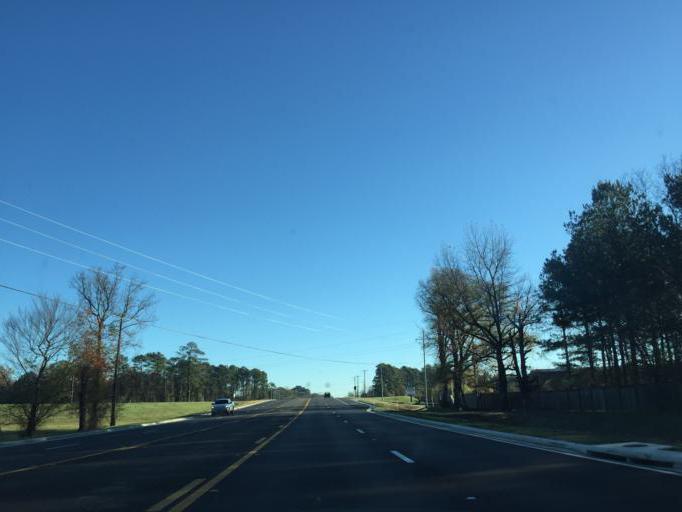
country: US
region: Mississippi
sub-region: Rankin County
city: Flowood
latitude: 32.3177
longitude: -90.1333
